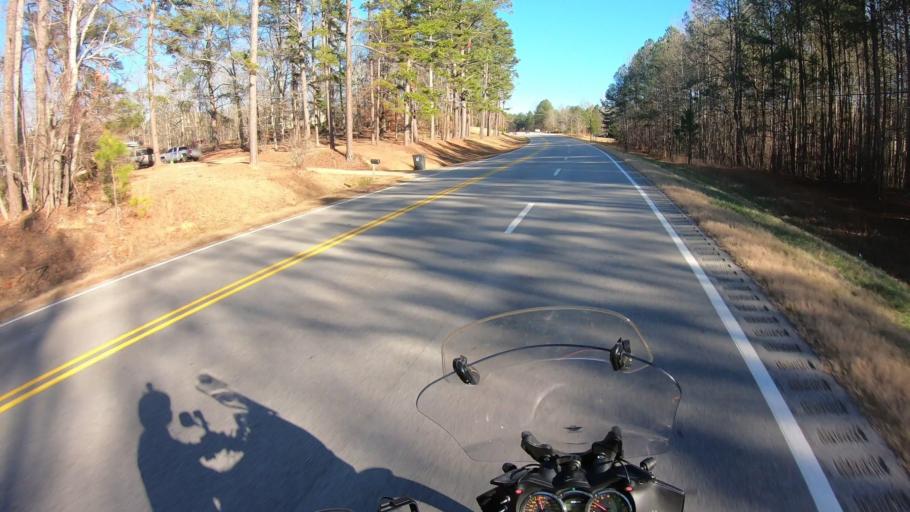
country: US
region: Alabama
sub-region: Cleburne County
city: Heflin
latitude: 33.6800
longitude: -85.5332
